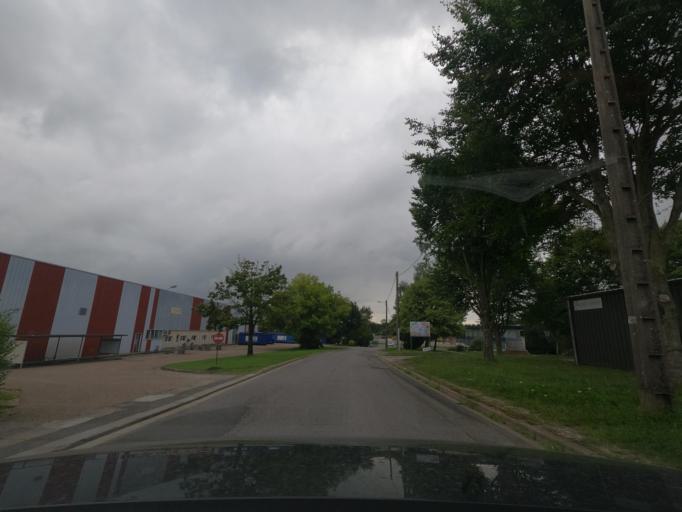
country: FR
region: Haute-Normandie
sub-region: Departement de la Seine-Maritime
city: Forges-les-Eaux
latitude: 49.6117
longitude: 1.5542
